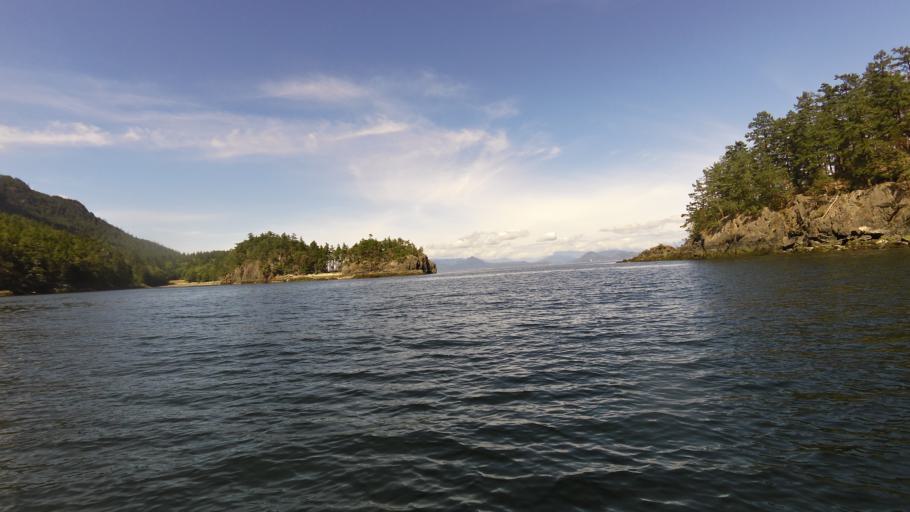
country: CA
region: British Columbia
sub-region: Regional District of Nanaimo
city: Parksville
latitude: 49.5139
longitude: -124.1337
